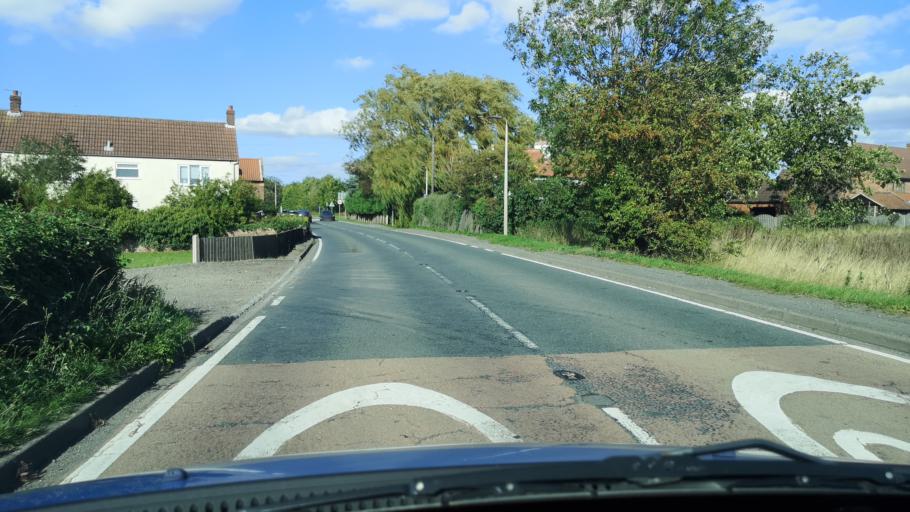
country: GB
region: England
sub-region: North Lincolnshire
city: Belton
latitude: 53.5620
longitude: -0.8188
